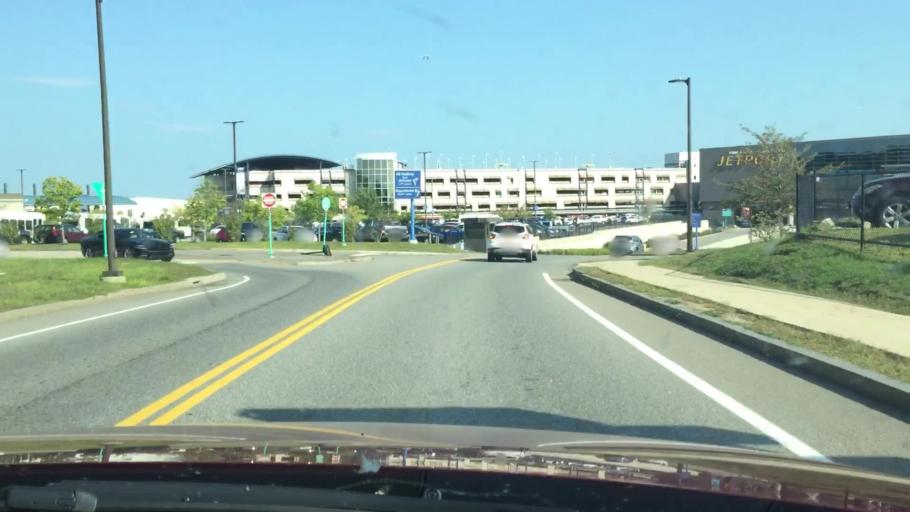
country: US
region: Maine
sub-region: Cumberland County
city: South Portland Gardens
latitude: 43.6495
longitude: -70.3136
